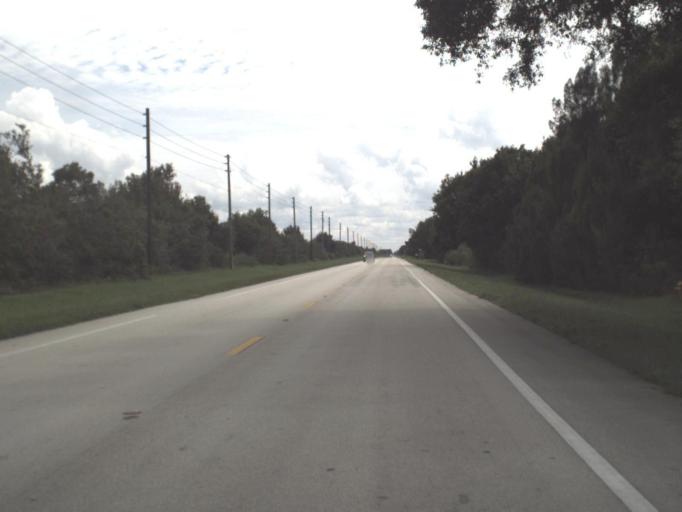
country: US
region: Florida
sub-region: DeSoto County
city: Southeast Arcadia
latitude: 27.1635
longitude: -81.8194
